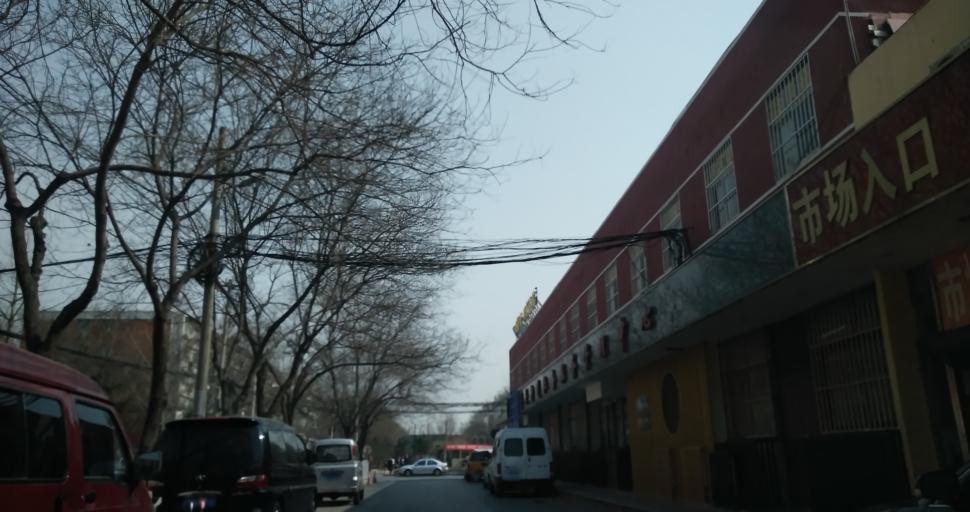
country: CN
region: Beijing
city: Dongfeng
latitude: 39.8661
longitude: 116.5035
